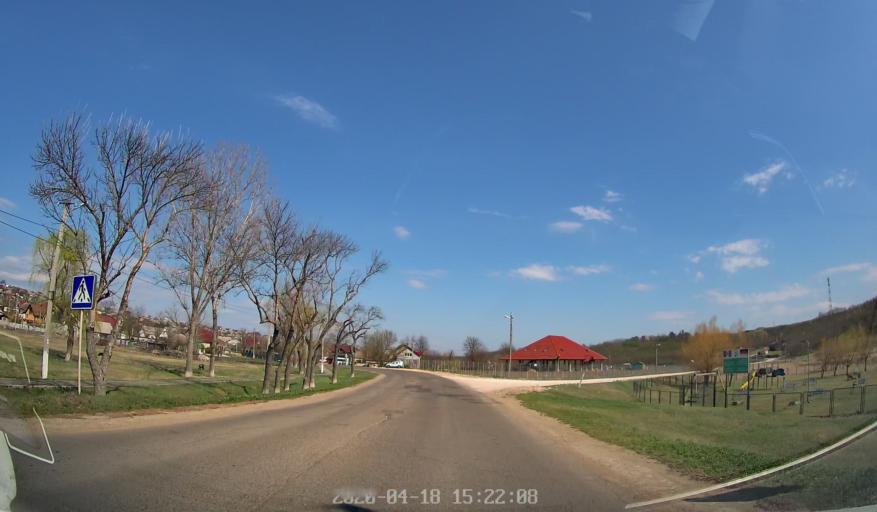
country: MD
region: Chisinau
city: Vadul lui Voda
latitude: 47.0623
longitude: 29.0041
